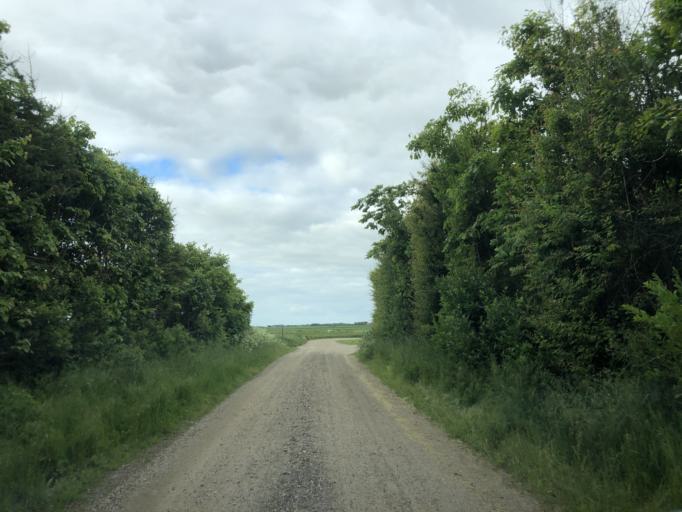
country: DK
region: Central Jutland
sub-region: Holstebro Kommune
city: Ulfborg
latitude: 56.2287
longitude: 8.1937
